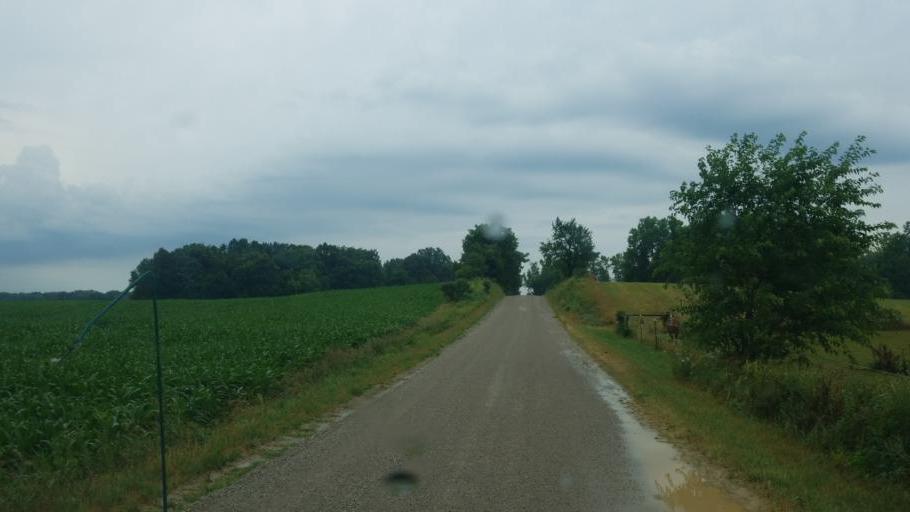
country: US
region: Indiana
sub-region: Steuben County
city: Hamilton
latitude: 41.5195
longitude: -84.9313
